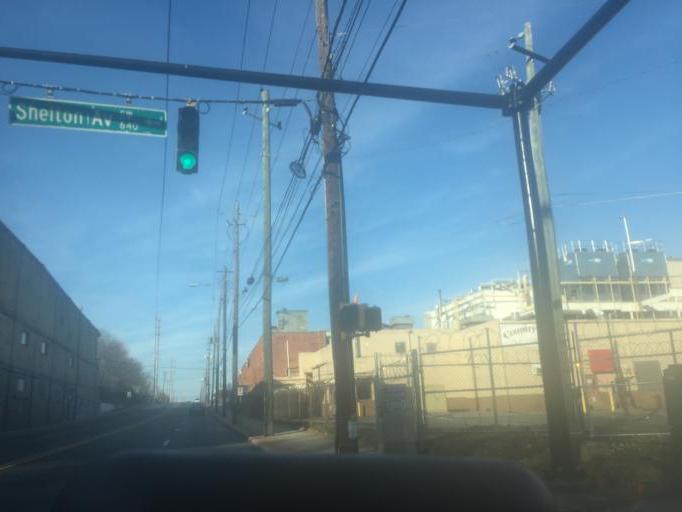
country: US
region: Georgia
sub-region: Fulton County
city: Atlanta
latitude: 33.7344
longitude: -84.4081
